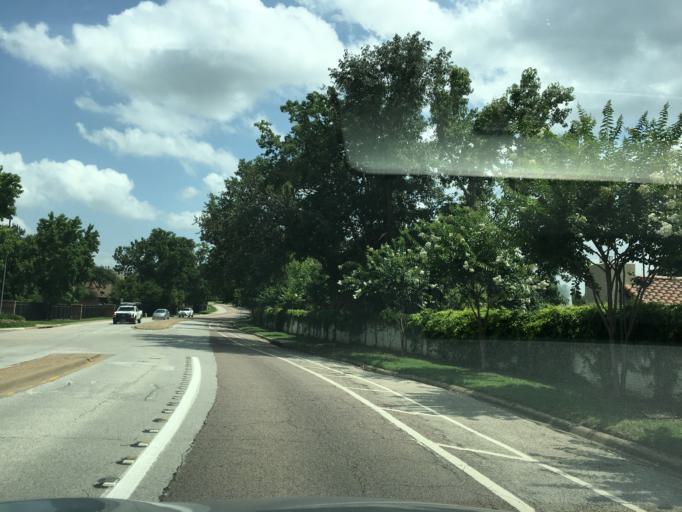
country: US
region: Texas
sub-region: Dallas County
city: University Park
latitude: 32.8768
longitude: -96.7789
